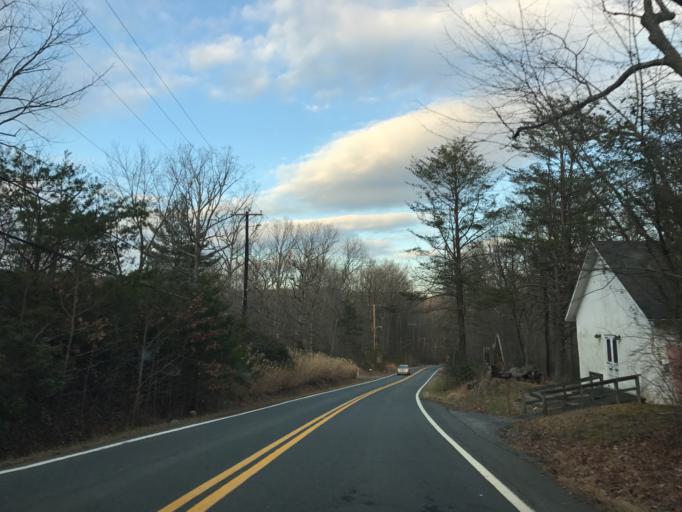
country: US
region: Maryland
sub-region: Cecil County
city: Charlestown
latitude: 39.4981
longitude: -75.9686
